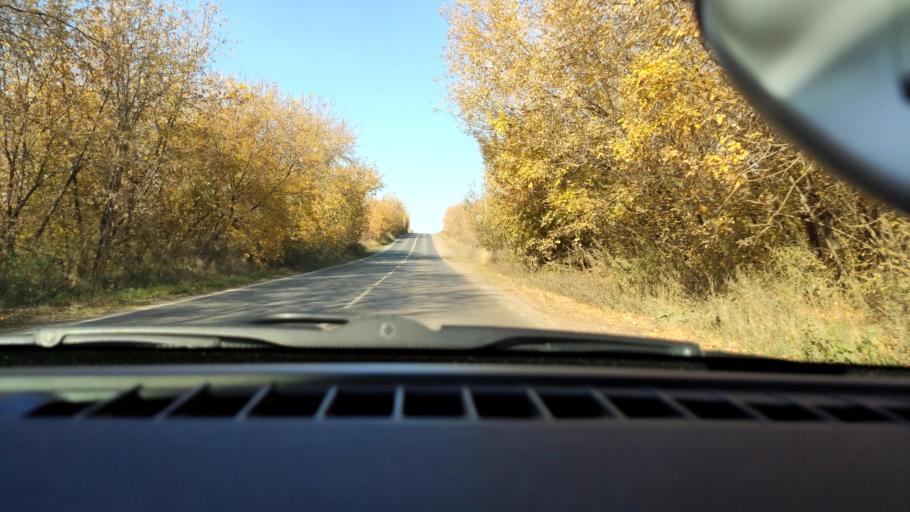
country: RU
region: Perm
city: Gamovo
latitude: 57.9081
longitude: 56.1651
